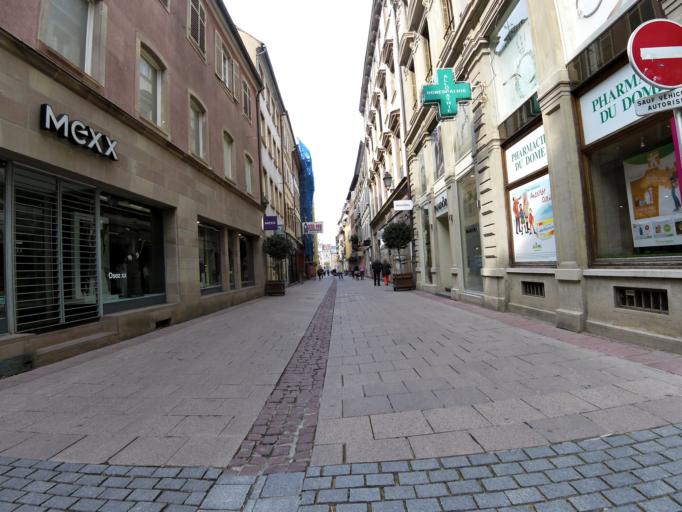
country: FR
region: Alsace
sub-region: Departement du Bas-Rhin
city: Strasbourg
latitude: 48.5827
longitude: 7.7511
